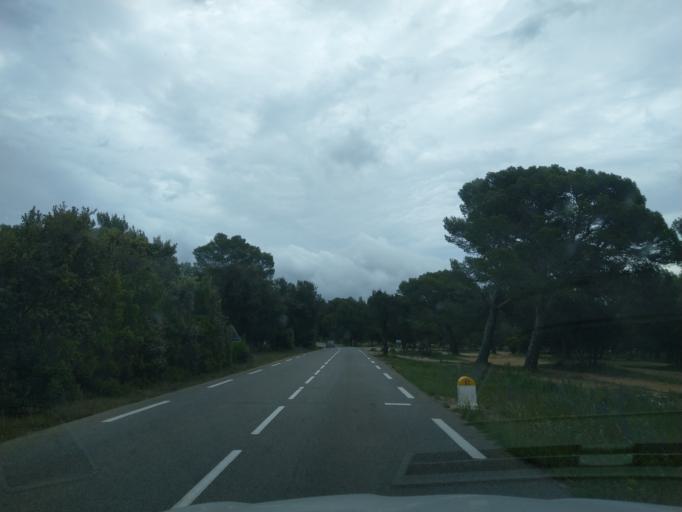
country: FR
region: Provence-Alpes-Cote d'Azur
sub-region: Departement du Var
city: Le Castellet
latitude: 43.2655
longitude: 5.7718
